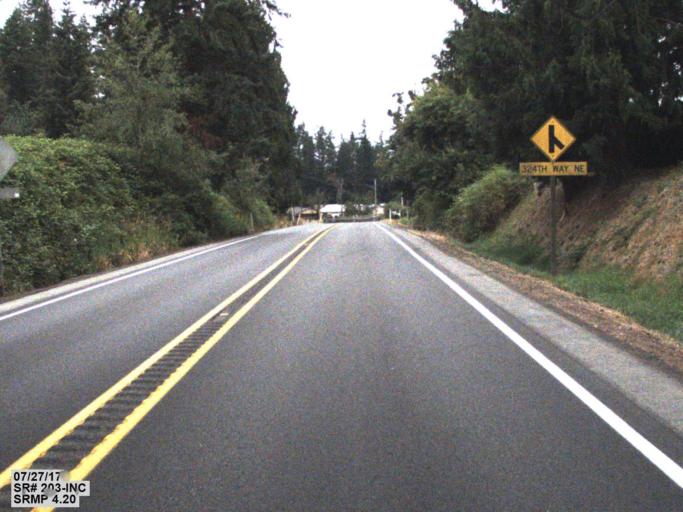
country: US
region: Washington
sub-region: King County
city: Carnation
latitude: 47.6234
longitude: -121.9097
